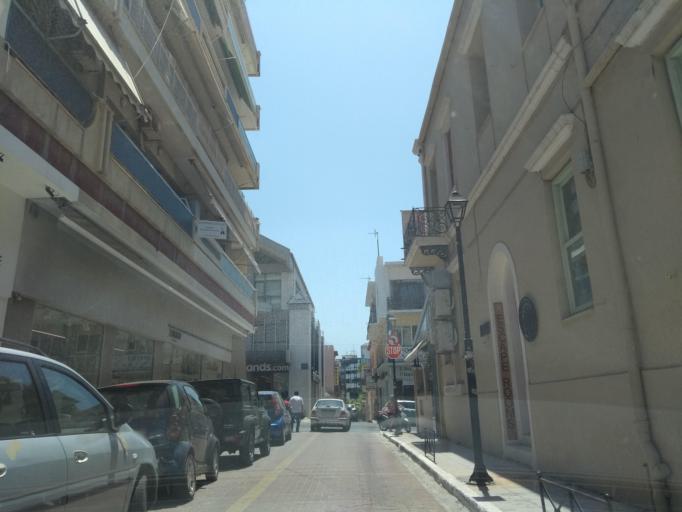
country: GR
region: Crete
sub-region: Nomos Chanias
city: Chania
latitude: 35.5130
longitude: 24.0226
